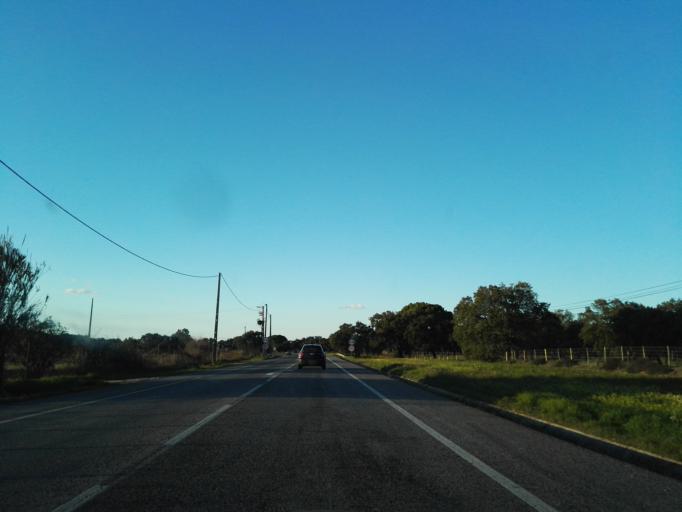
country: PT
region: Santarem
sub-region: Benavente
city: Samora Correia
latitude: 38.9063
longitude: -8.8442
